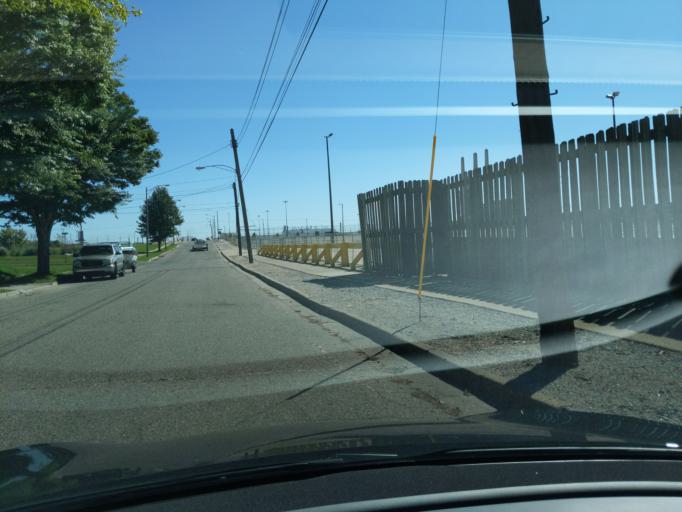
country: US
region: Michigan
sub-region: Ingham County
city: Lansing
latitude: 42.7244
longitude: -84.5719
